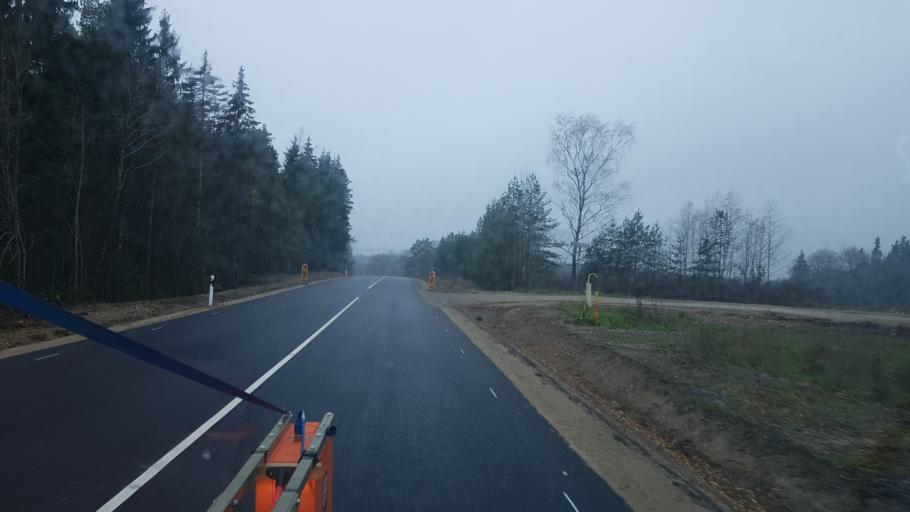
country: EE
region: Raplamaa
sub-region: Kohila vald
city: Kohila
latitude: 59.1785
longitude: 24.8228
